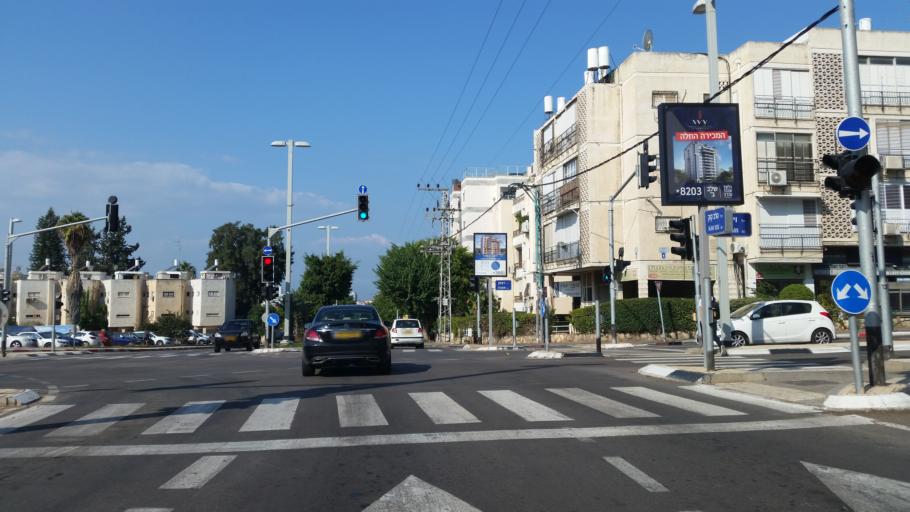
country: IL
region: Tel Aviv
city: Herzliyya
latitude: 32.1624
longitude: 34.8348
